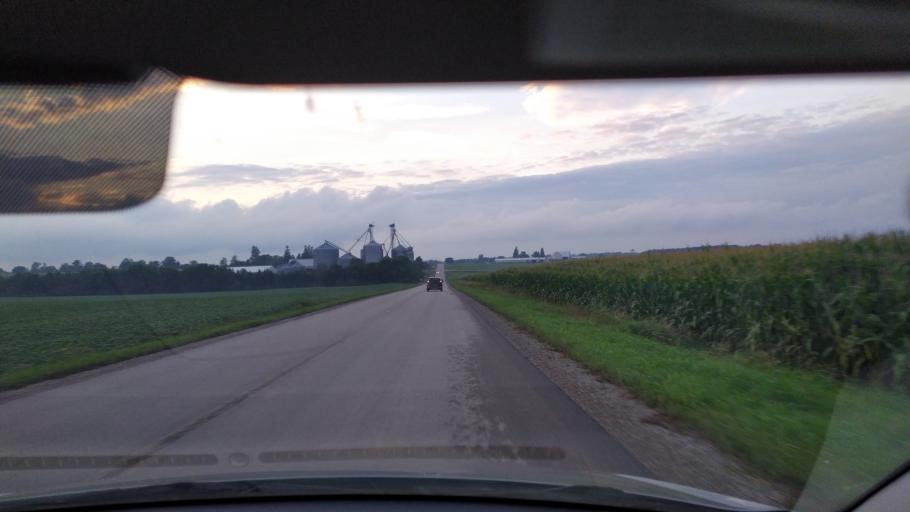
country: CA
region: Ontario
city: Kitchener
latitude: 43.3311
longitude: -80.6219
